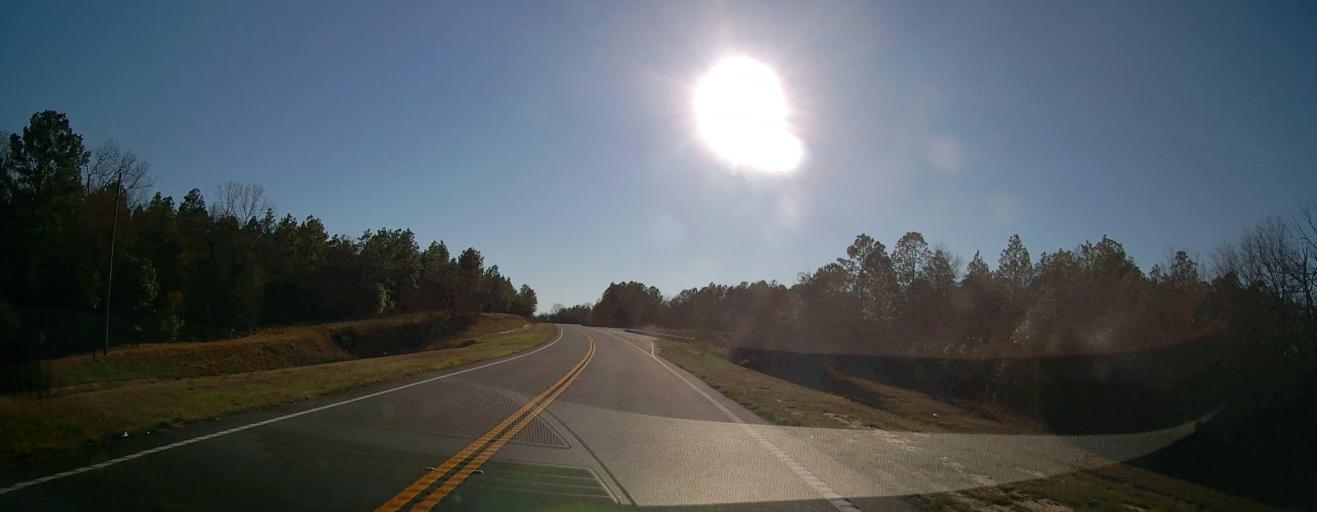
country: US
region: Georgia
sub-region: Taylor County
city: Butler
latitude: 32.5242
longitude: -84.3121
